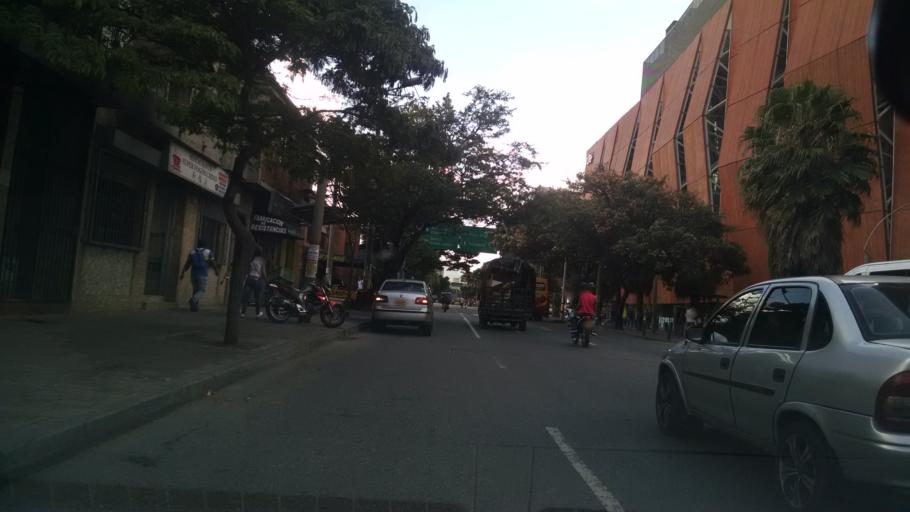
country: CO
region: Antioquia
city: Medellin
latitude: 6.2657
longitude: -75.5662
